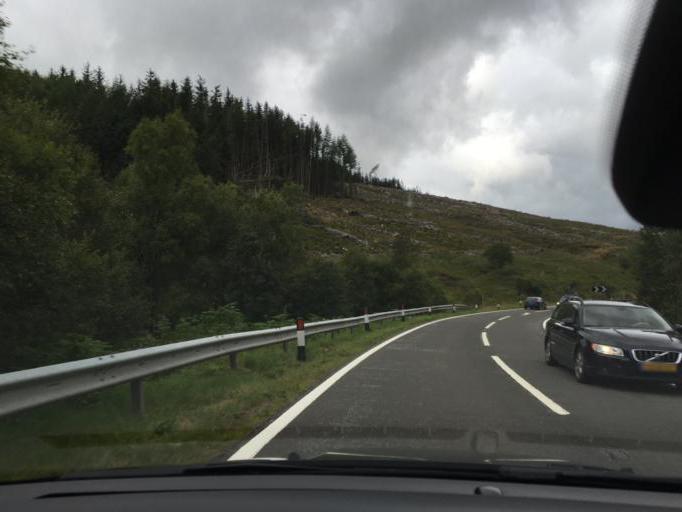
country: GB
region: Scotland
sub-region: Argyll and Bute
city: Garelochhead
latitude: 56.4660
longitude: -4.7247
